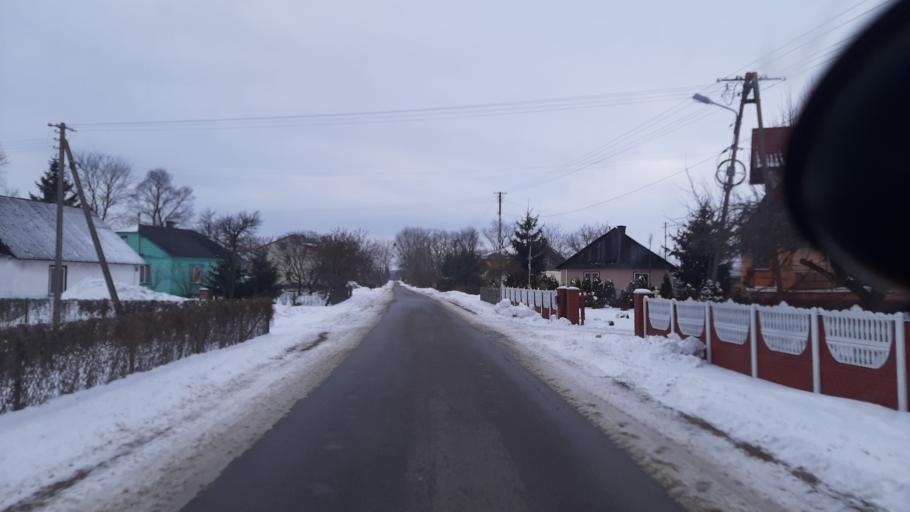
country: PL
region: Lublin Voivodeship
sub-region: Powiat lubartowski
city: Abramow
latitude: 51.4420
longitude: 22.2873
